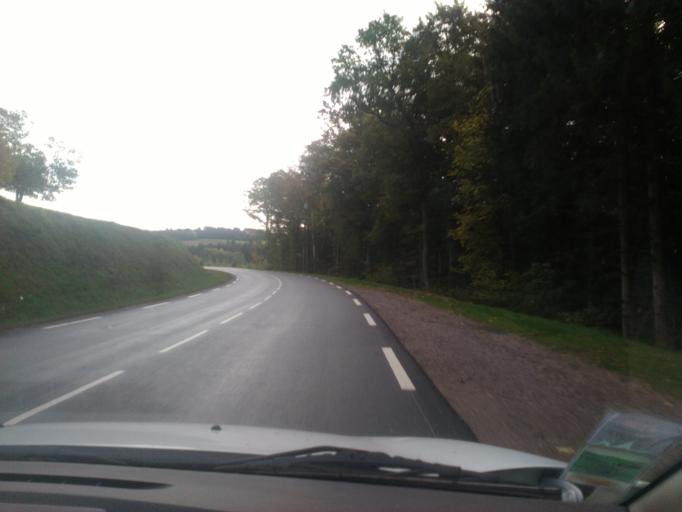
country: FR
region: Lorraine
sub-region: Departement des Vosges
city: Corcieux
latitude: 48.1636
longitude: 6.9053
